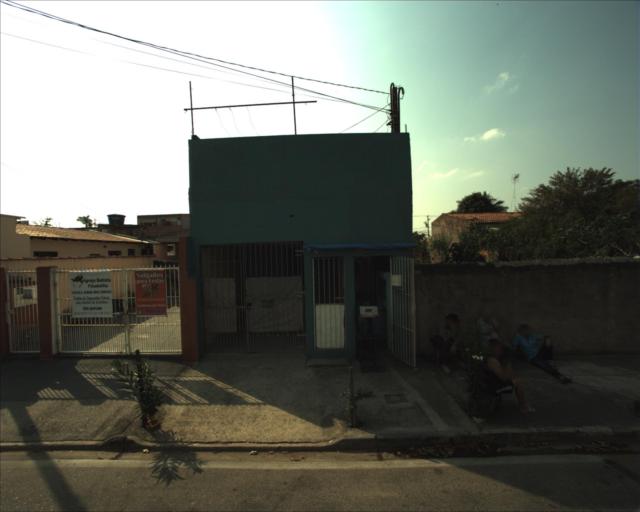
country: BR
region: Sao Paulo
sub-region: Sorocaba
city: Sorocaba
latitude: -23.4333
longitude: -47.4578
